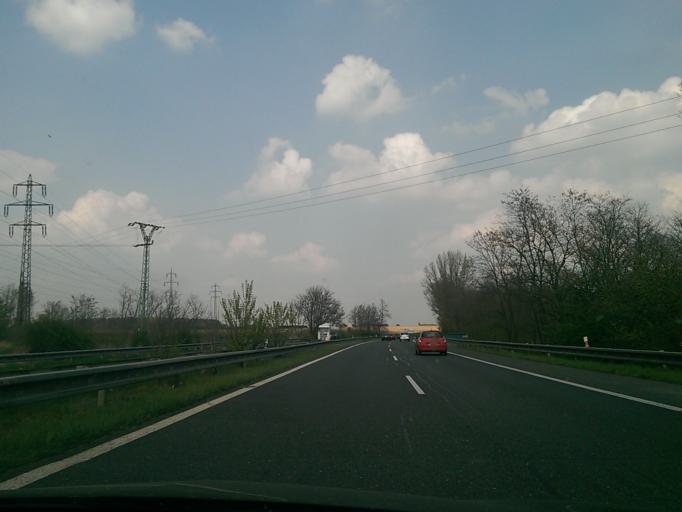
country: CZ
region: Central Bohemia
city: Benatky nad Jizerou
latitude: 50.2583
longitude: 14.7742
